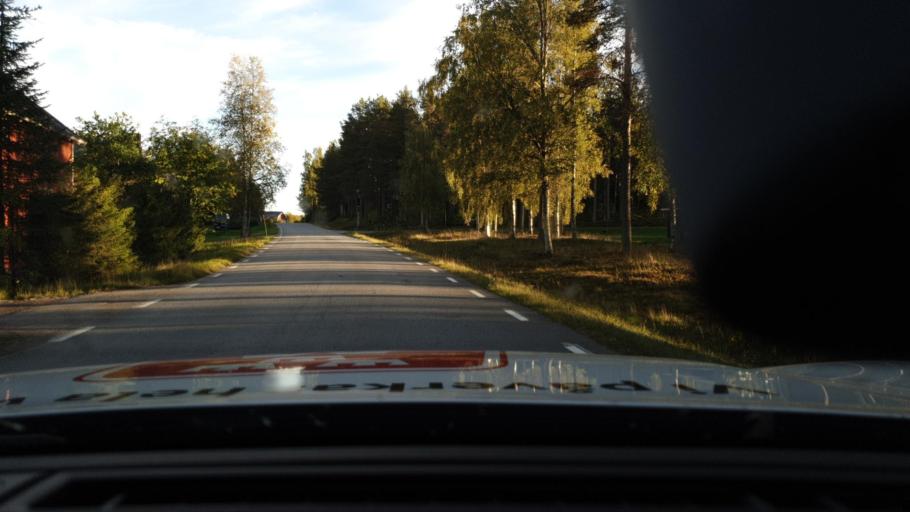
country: SE
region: Norrbotten
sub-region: Kalix Kommun
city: Toere
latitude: 65.8476
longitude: 22.6776
